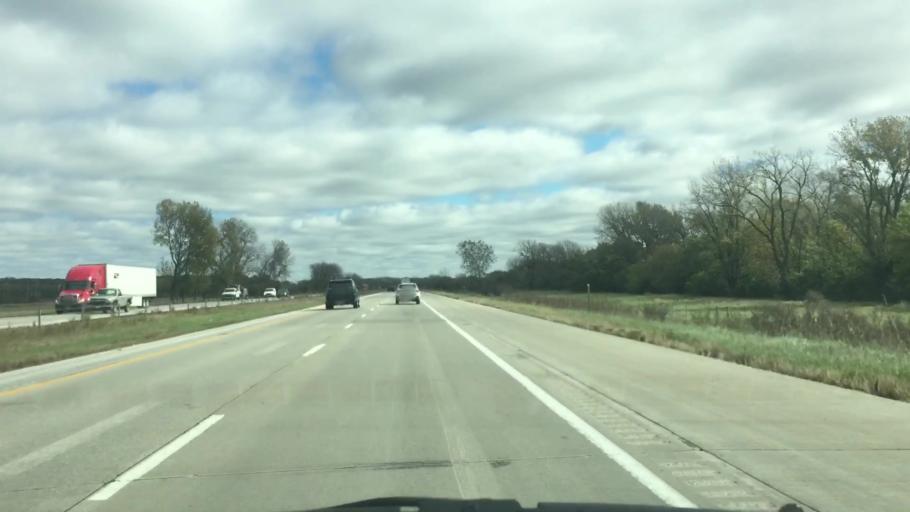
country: US
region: Iowa
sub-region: Polk County
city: Mitchellville
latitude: 41.6815
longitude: -93.3163
